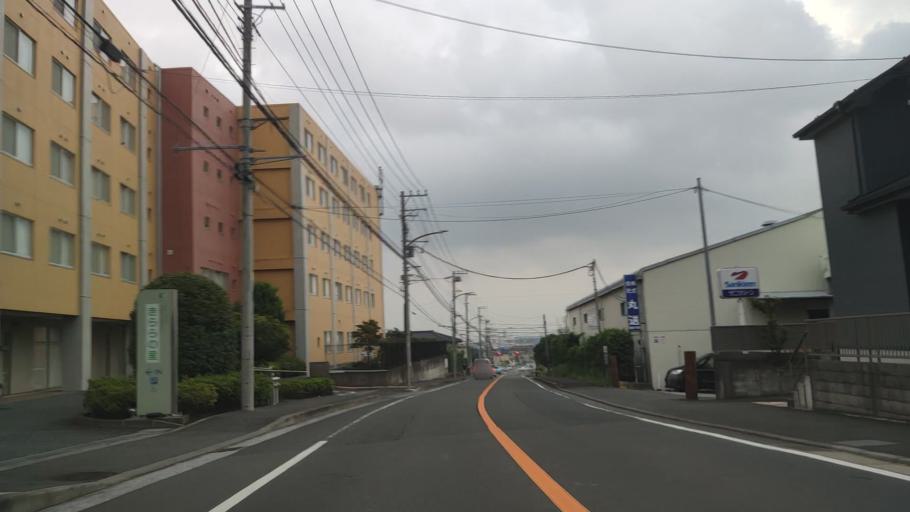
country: JP
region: Kanagawa
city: Minami-rinkan
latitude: 35.4252
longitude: 139.5019
